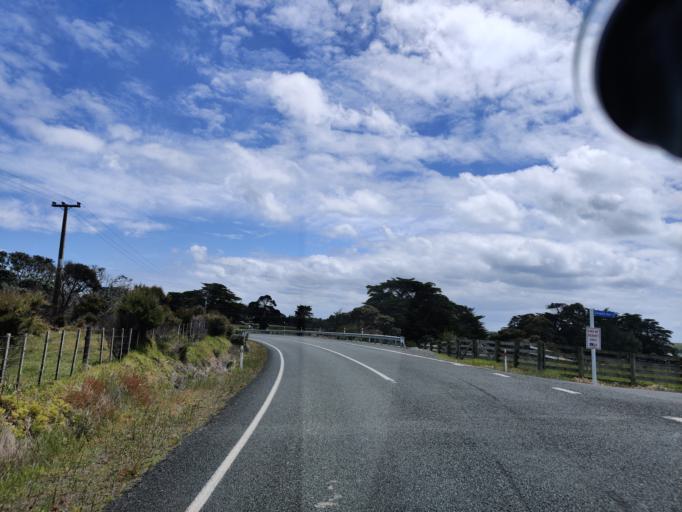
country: NZ
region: Northland
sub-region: Far North District
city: Kaitaia
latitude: -34.7974
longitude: 173.1080
